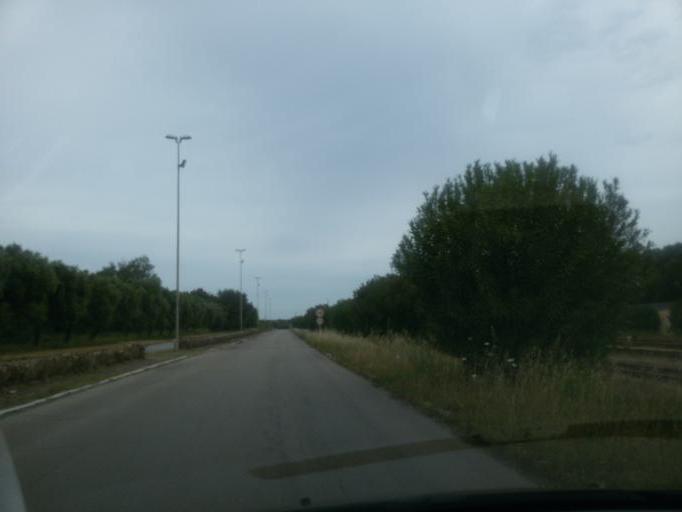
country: IT
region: Apulia
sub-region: Provincia di Brindisi
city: Materdomini
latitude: 40.6429
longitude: 17.9860
